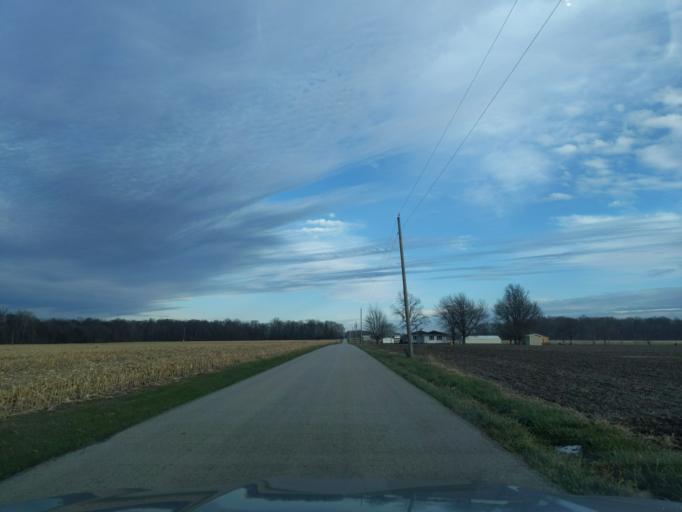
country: US
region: Indiana
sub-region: Decatur County
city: Westport
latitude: 39.2192
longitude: -85.4977
